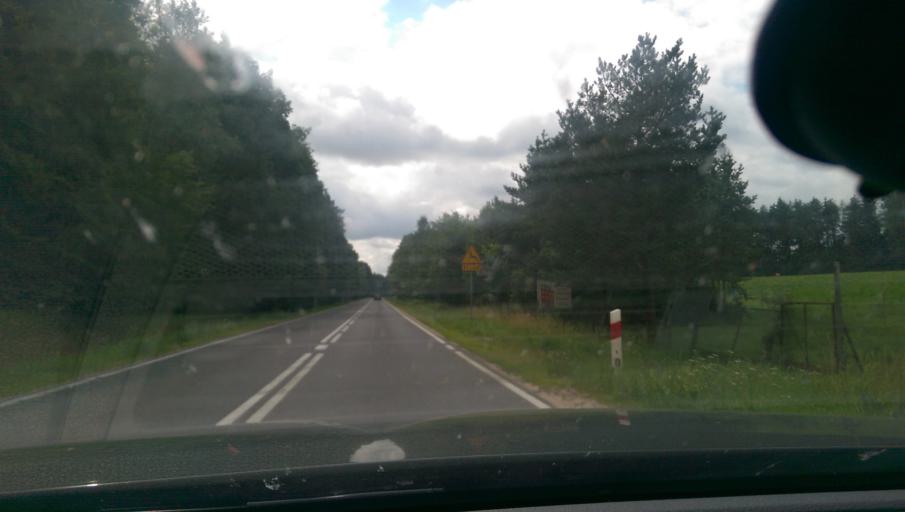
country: PL
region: Warmian-Masurian Voivodeship
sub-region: Powiat goldapski
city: Goldap
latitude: 54.3326
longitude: 22.2949
